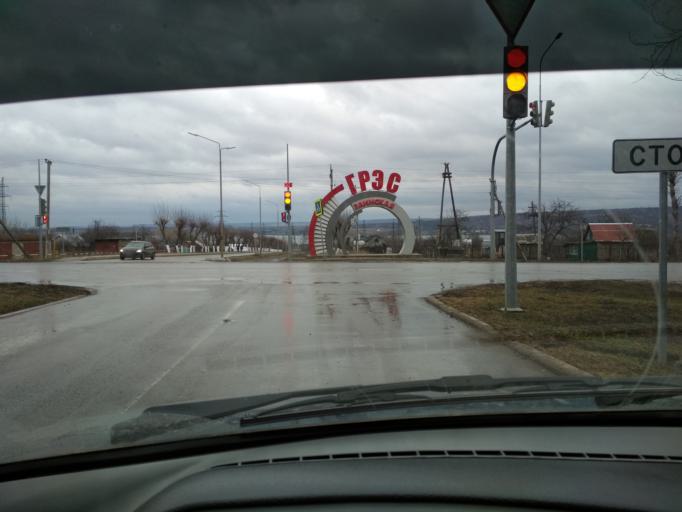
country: RU
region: Tatarstan
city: Zainsk
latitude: 55.2828
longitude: 52.0085
